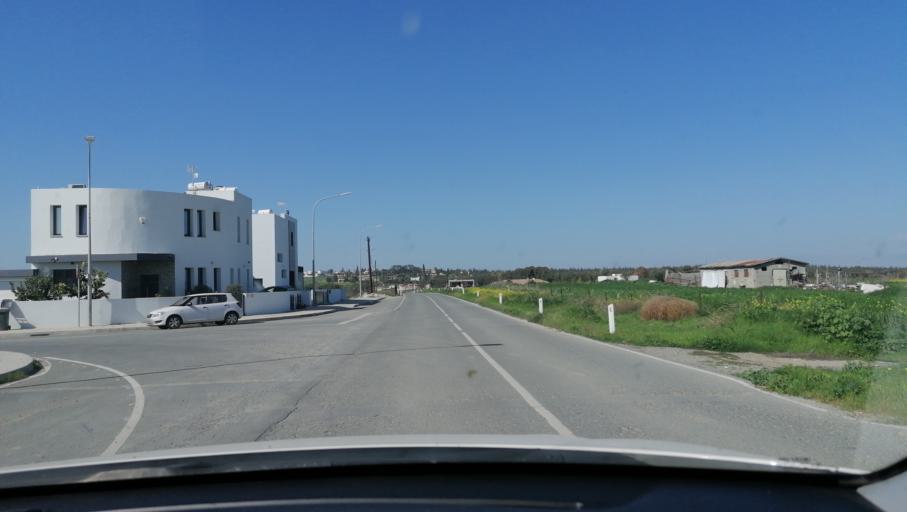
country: CY
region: Lefkosia
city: Geri
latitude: 35.1182
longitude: 33.4037
